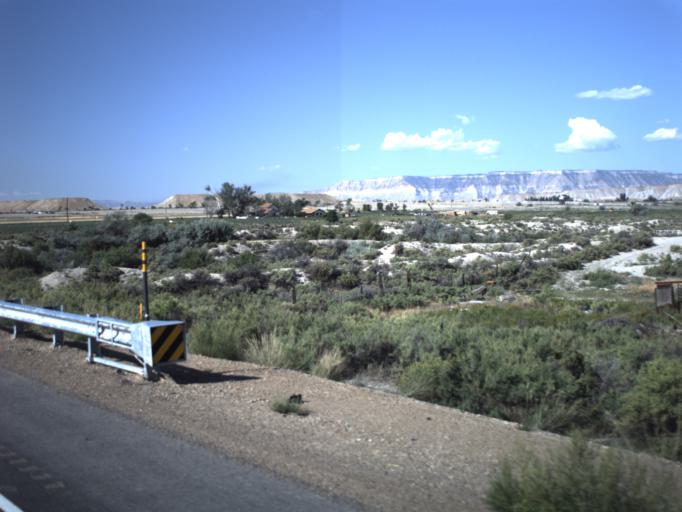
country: US
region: Utah
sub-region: Emery County
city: Huntington
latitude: 39.2976
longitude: -110.9651
